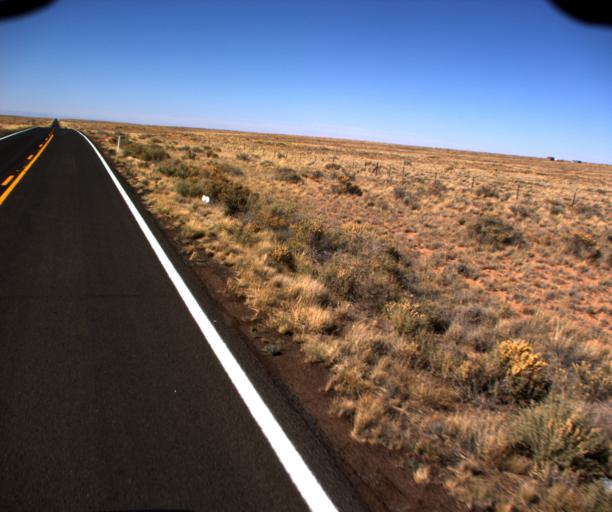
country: US
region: Arizona
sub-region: Coconino County
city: Tuba City
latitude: 35.9604
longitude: -110.9380
